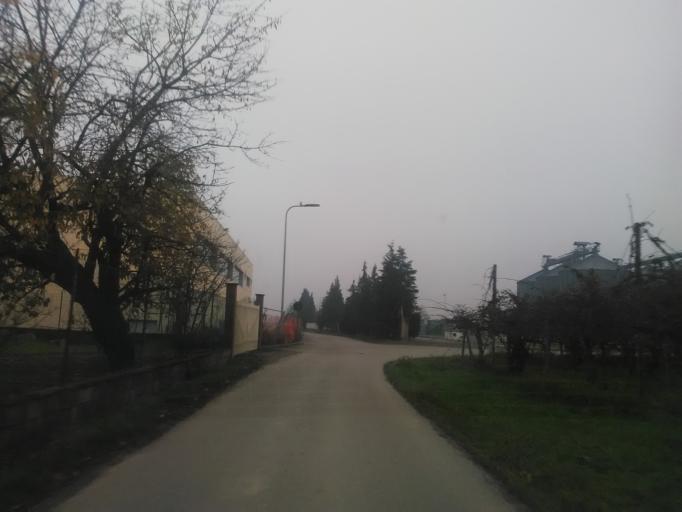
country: IT
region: Piedmont
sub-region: Provincia di Vercelli
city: Moncrivello
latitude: 45.3263
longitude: 8.0048
